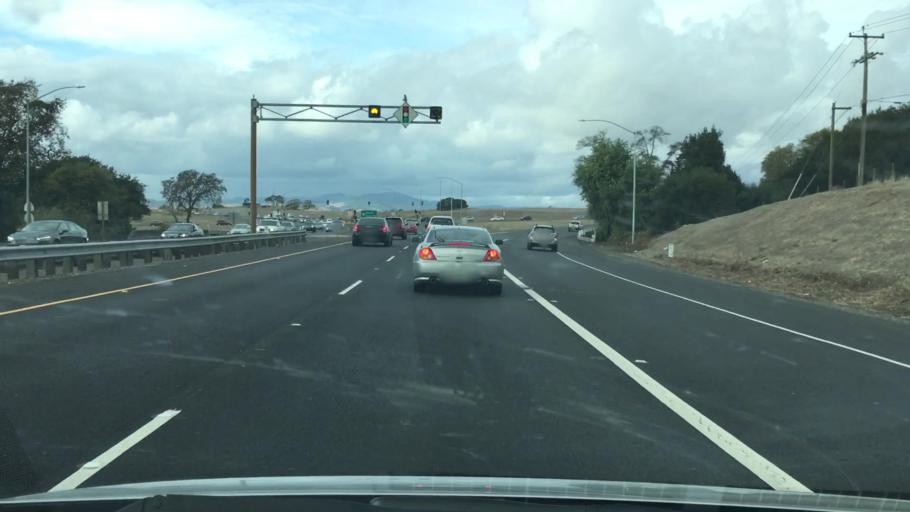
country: US
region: California
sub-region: Napa County
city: Napa
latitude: 38.2398
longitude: -122.2667
